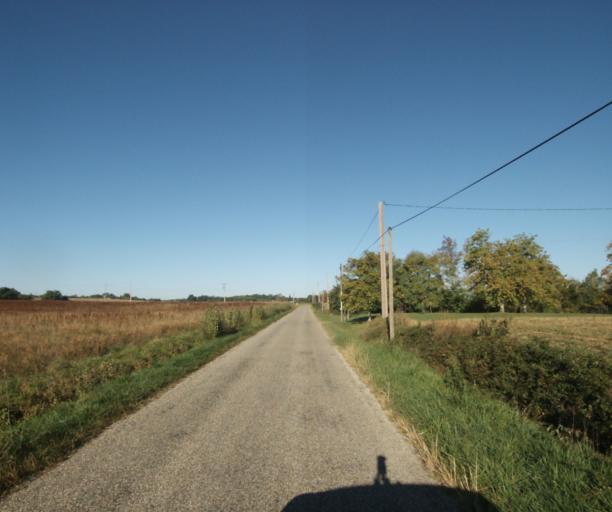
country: FR
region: Midi-Pyrenees
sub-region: Departement du Gers
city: Gondrin
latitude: 43.8483
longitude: 0.2360
